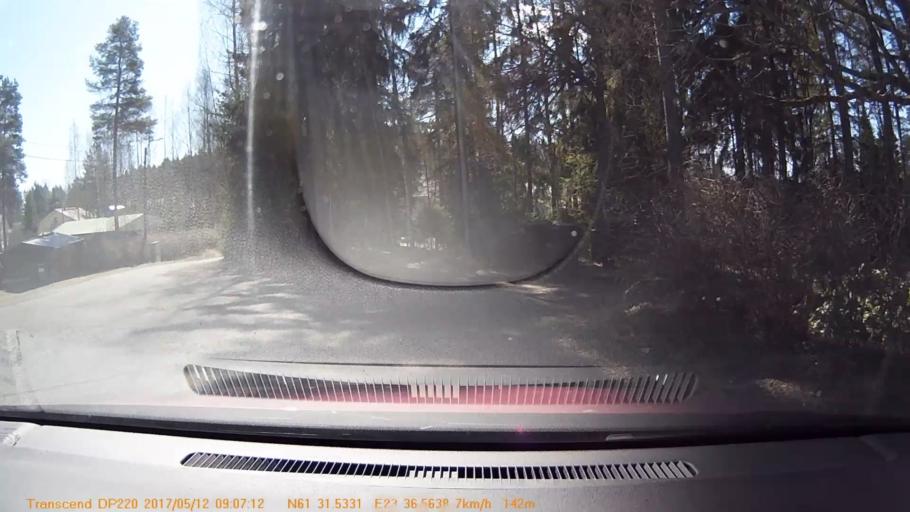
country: FI
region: Pirkanmaa
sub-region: Tampere
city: Yloejaervi
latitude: 61.5256
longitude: 23.6094
